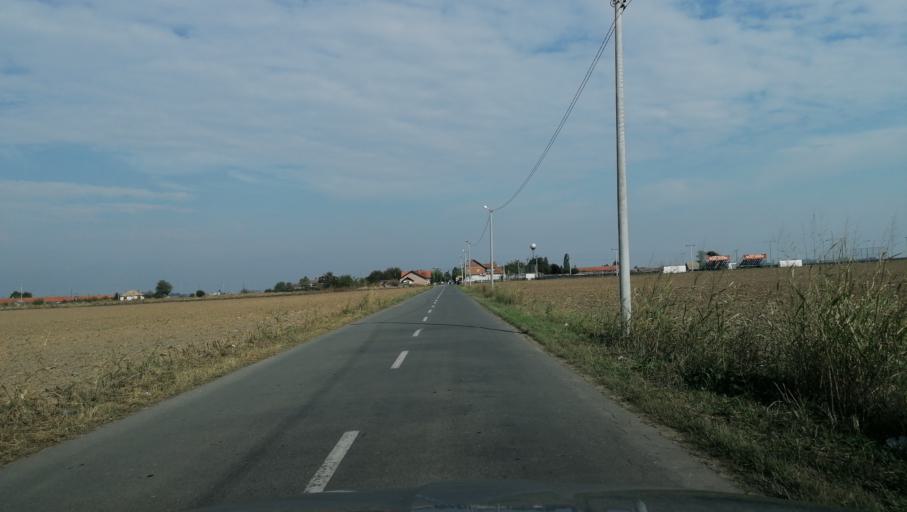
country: BA
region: Republika Srpska
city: Bijeljina
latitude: 44.7688
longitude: 19.2454
